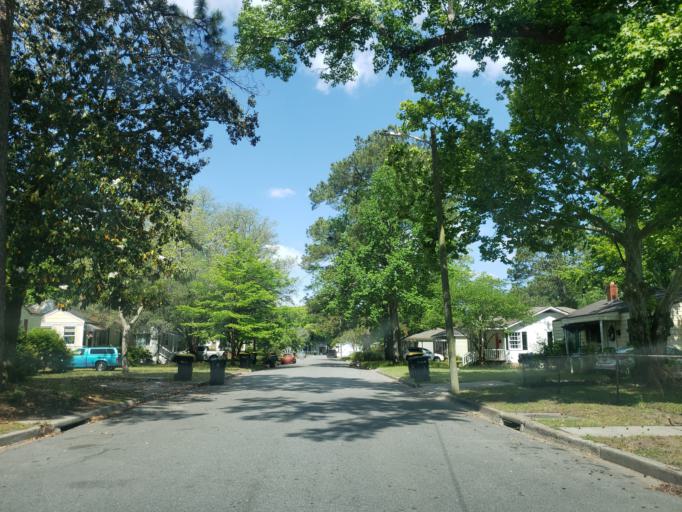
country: US
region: Georgia
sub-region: Chatham County
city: Thunderbolt
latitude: 32.0661
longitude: -81.0543
